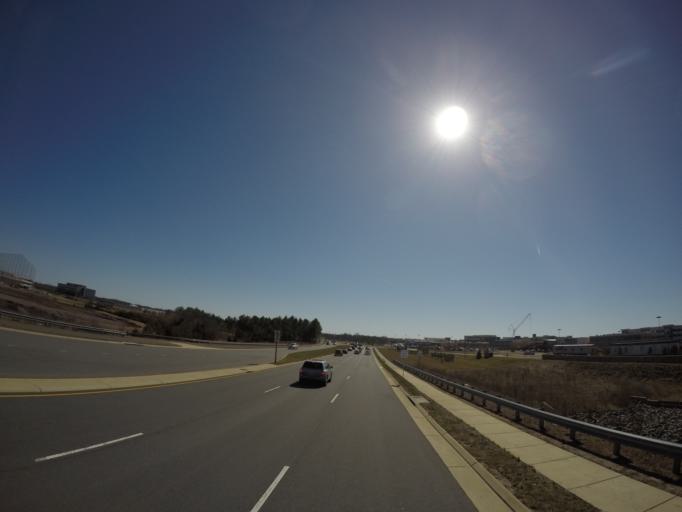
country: US
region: Virginia
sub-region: Loudoun County
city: University Center
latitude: 39.0543
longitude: -77.4514
